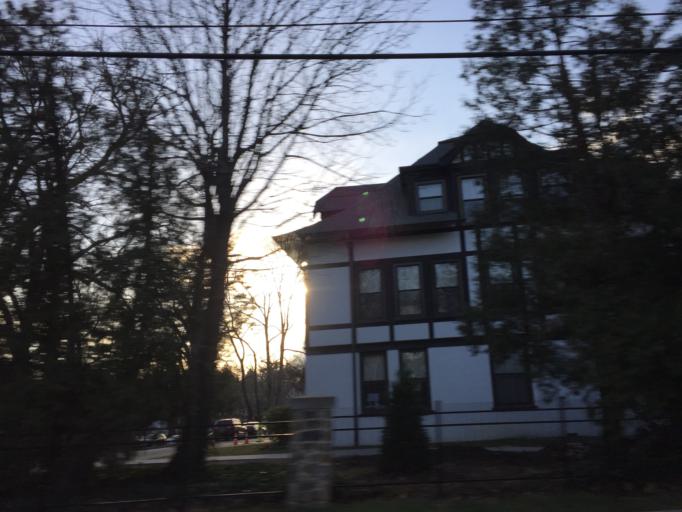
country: US
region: New Jersey
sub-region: Union County
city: Summit
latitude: 40.7207
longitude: -74.3637
